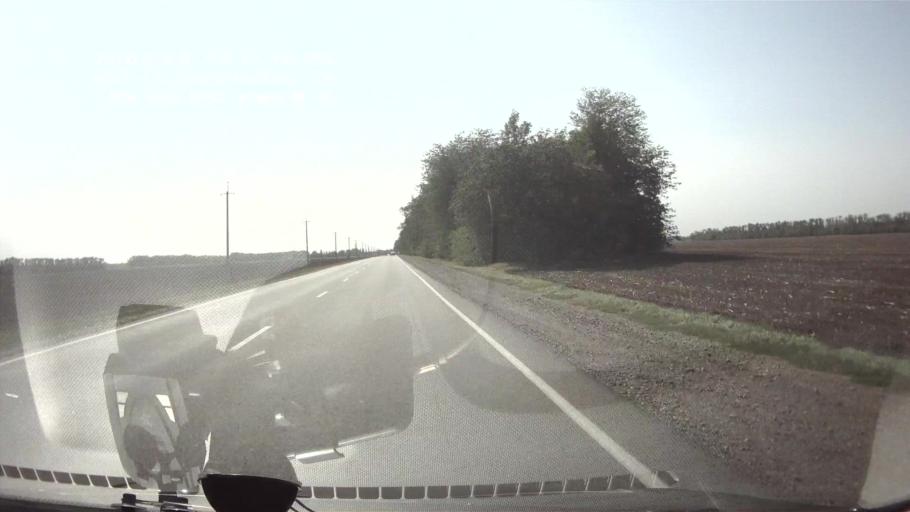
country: RU
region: Krasnodarskiy
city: Kavkazskaya
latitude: 45.4785
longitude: 40.6796
